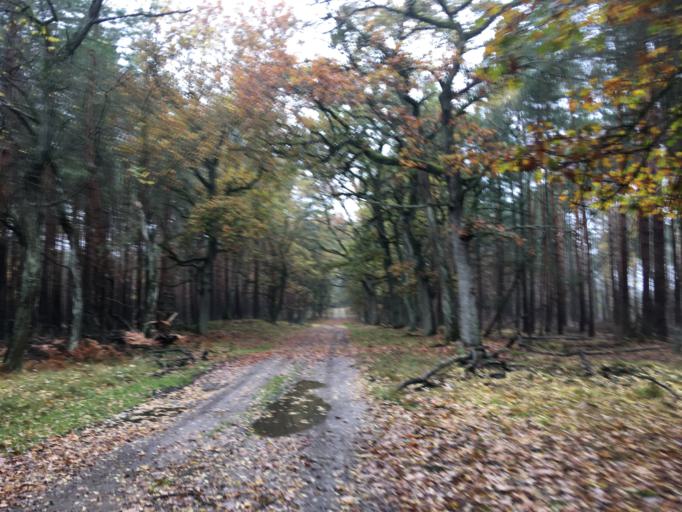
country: DE
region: Brandenburg
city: Beeskow
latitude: 52.2133
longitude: 14.3005
